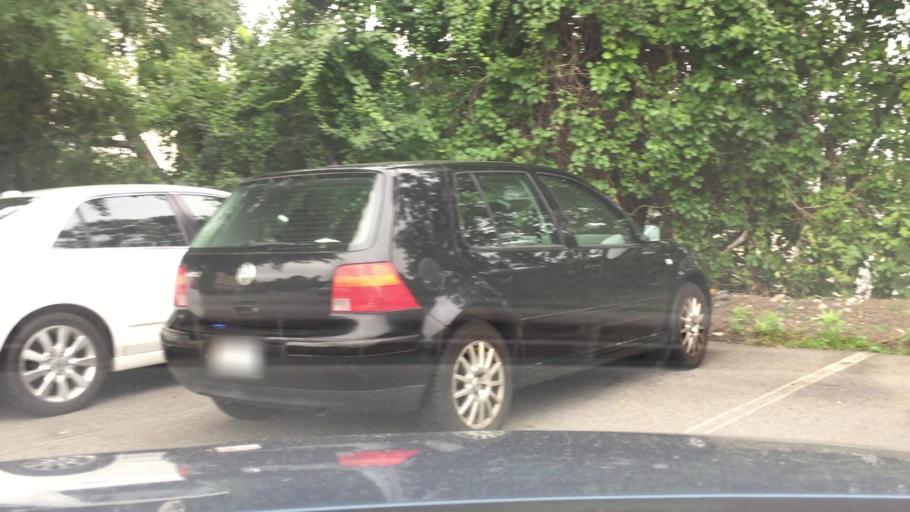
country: US
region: Massachusetts
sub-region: Middlesex County
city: Waltham
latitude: 42.3968
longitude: -71.2556
